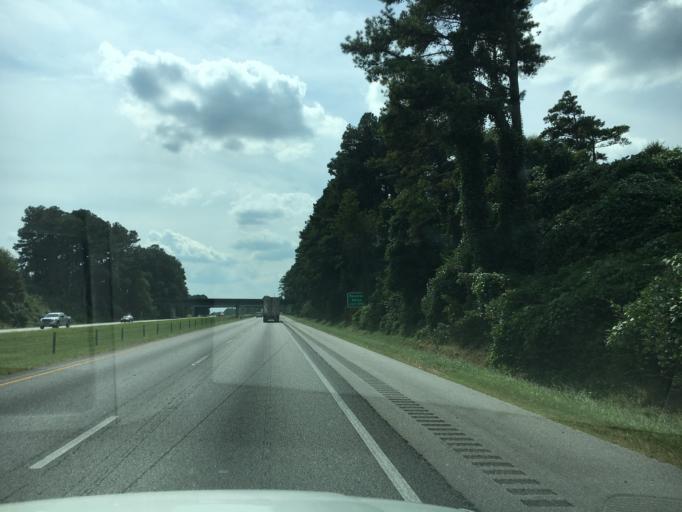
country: US
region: Georgia
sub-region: Franklin County
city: Lavonia
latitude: 34.4486
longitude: -83.1181
